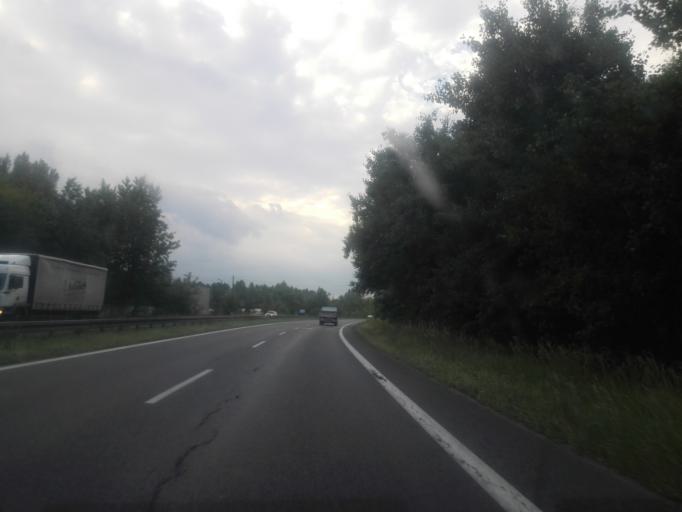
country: PL
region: Silesian Voivodeship
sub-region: Powiat bedzinski
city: Siewierz
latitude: 50.4843
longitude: 19.2189
